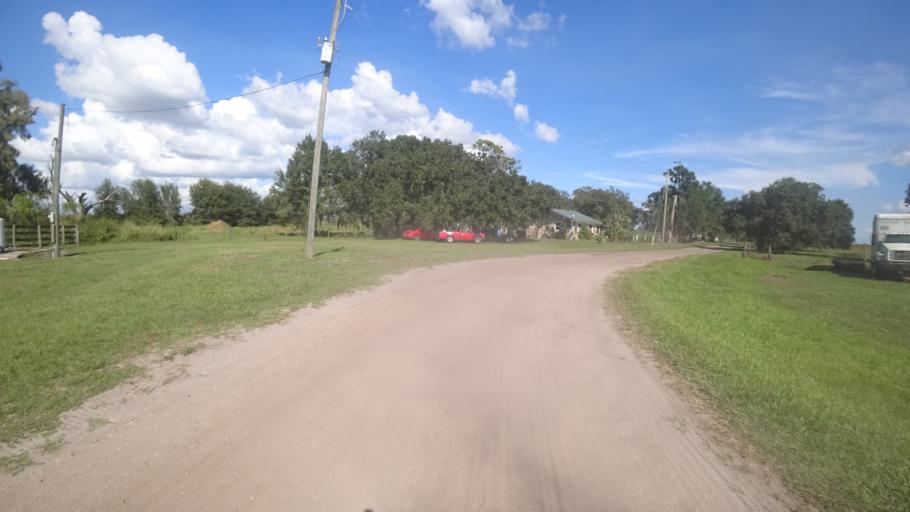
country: US
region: Florida
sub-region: DeSoto County
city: Arcadia
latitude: 27.3094
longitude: -82.0941
